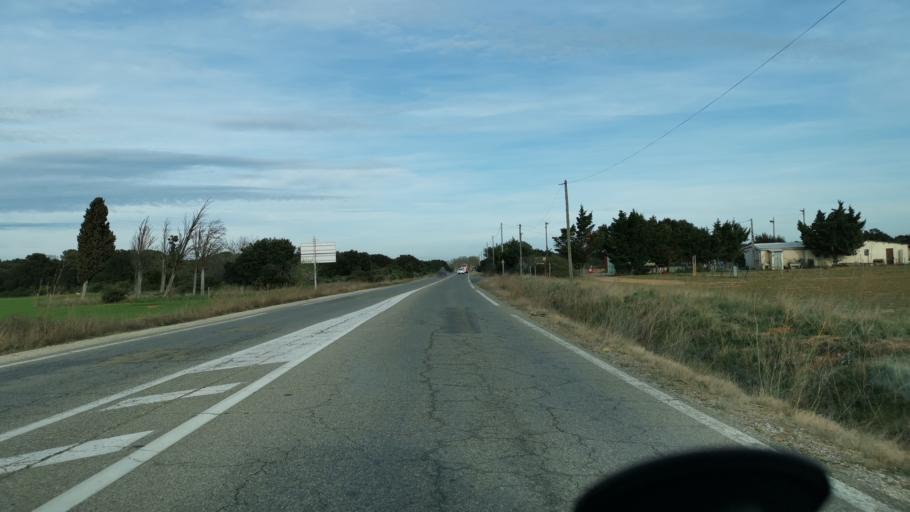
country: FR
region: Provence-Alpes-Cote d'Azur
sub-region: Departement des Bouches-du-Rhone
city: Saint-Martin-de-Crau
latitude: 43.6350
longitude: 4.7786
